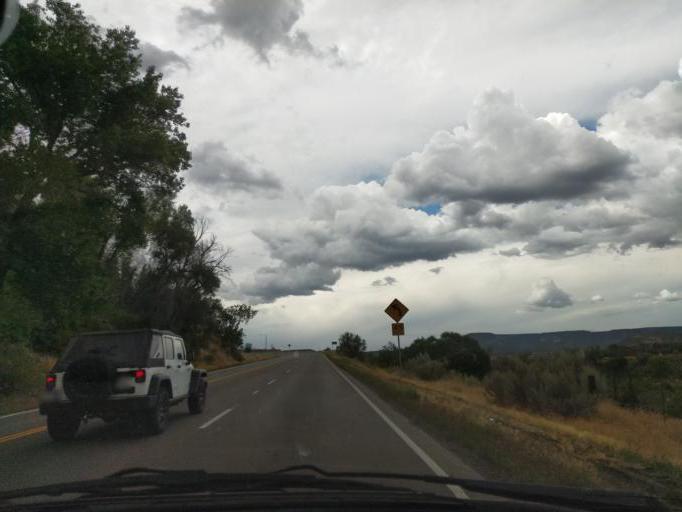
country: US
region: Colorado
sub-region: Delta County
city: Paonia
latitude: 38.8005
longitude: -107.7351
